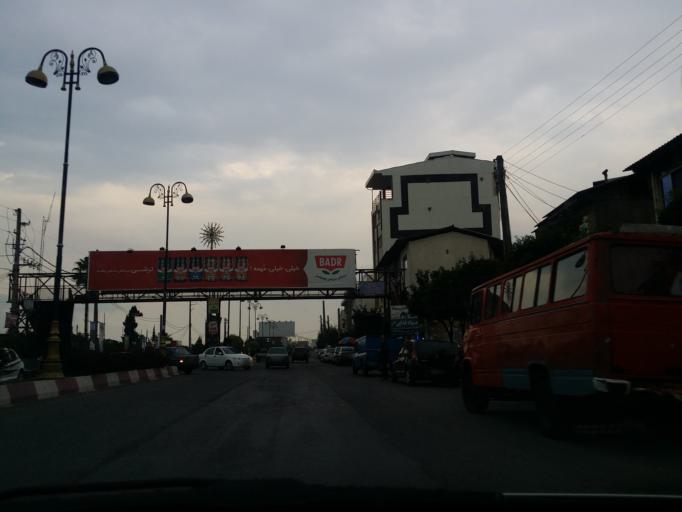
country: IR
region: Mazandaran
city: `Abbasabad
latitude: 36.7276
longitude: 51.1108
